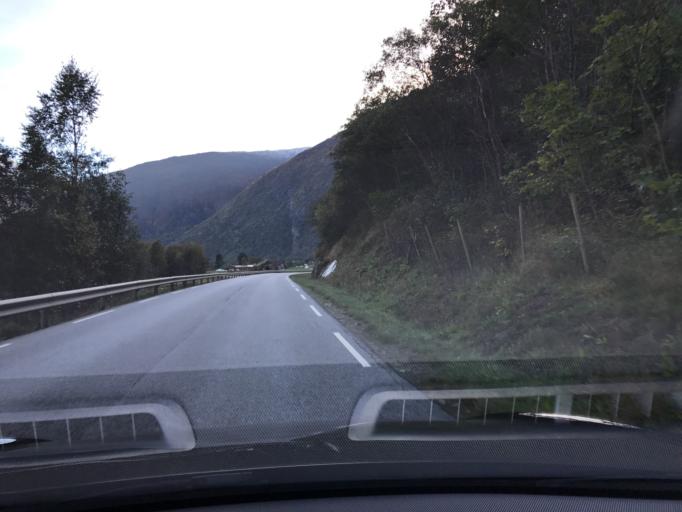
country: NO
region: Sogn og Fjordane
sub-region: Laerdal
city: Laerdalsoyri
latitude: 61.0910
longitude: 7.5160
